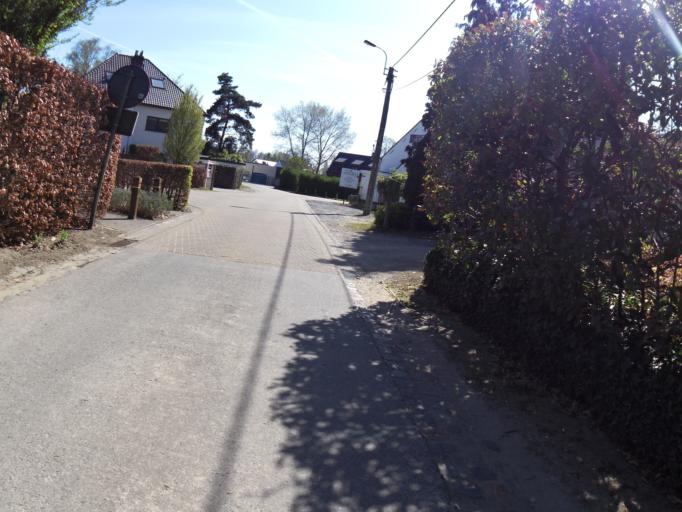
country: BE
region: Flanders
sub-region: Provincie Oost-Vlaanderen
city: Sint-Martens-Latem
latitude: 51.0086
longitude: 3.6284
